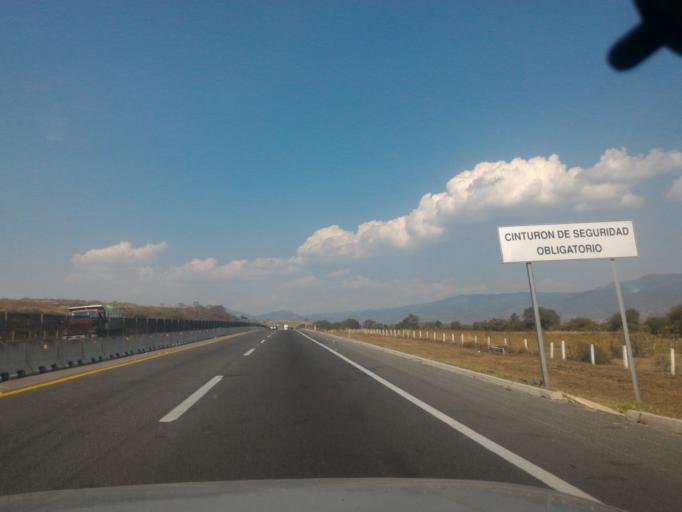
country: MX
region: Jalisco
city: Gomez Farias
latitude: 19.7802
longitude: -103.5111
